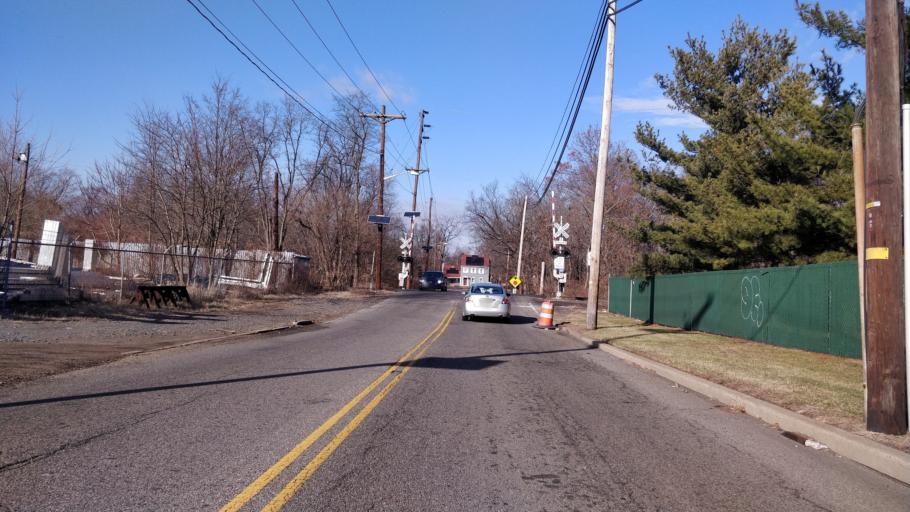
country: US
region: New Jersey
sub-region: Middlesex County
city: South Plainfield
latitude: 40.5812
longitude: -74.4301
